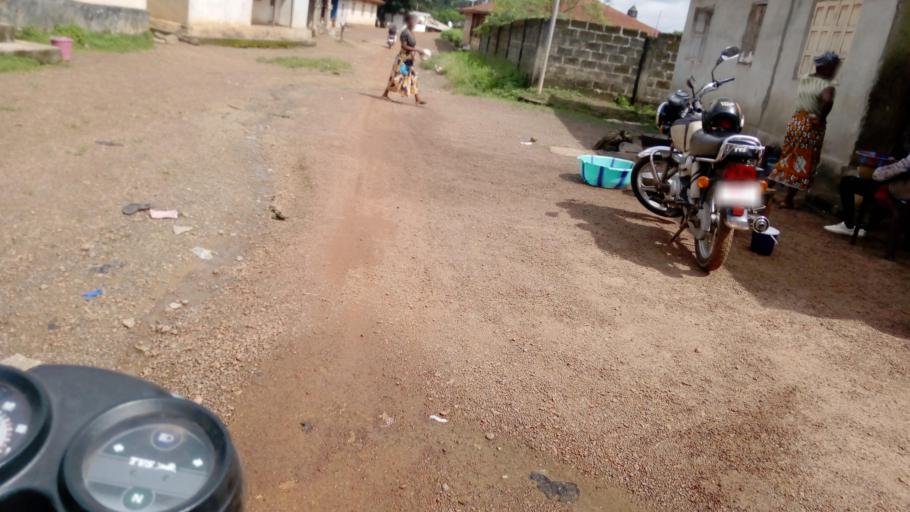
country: SL
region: Northern Province
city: Makeni
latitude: 8.8881
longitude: -12.0328
